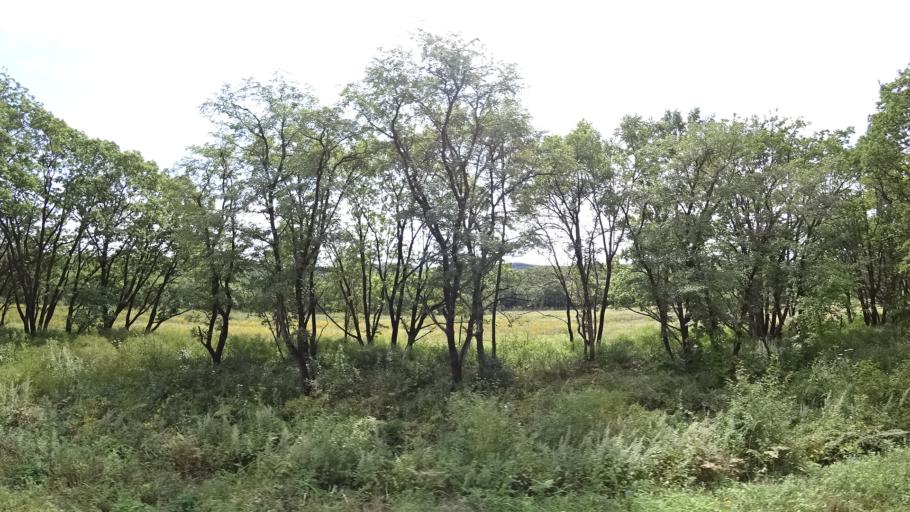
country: RU
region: Primorskiy
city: Lyalichi
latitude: 44.1403
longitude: 132.4110
